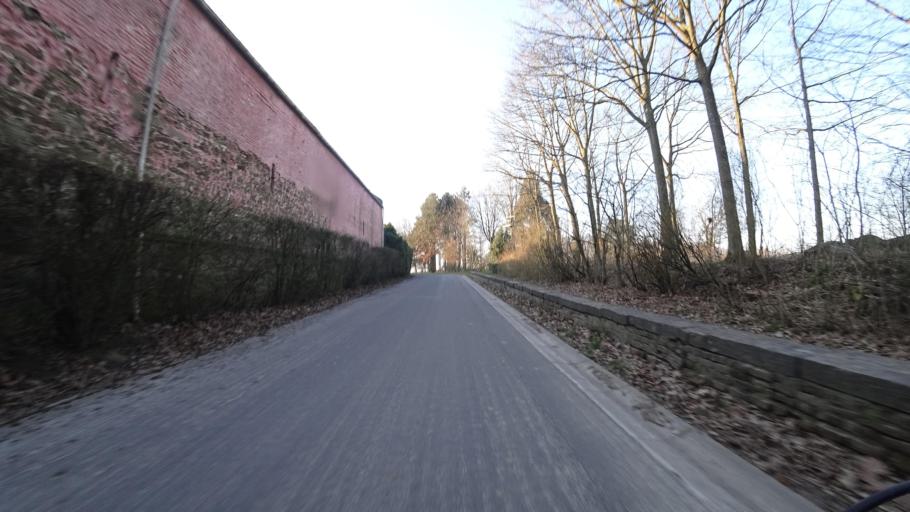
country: BE
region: Wallonia
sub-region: Province de Namur
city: Gembloux
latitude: 50.5811
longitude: 4.6684
